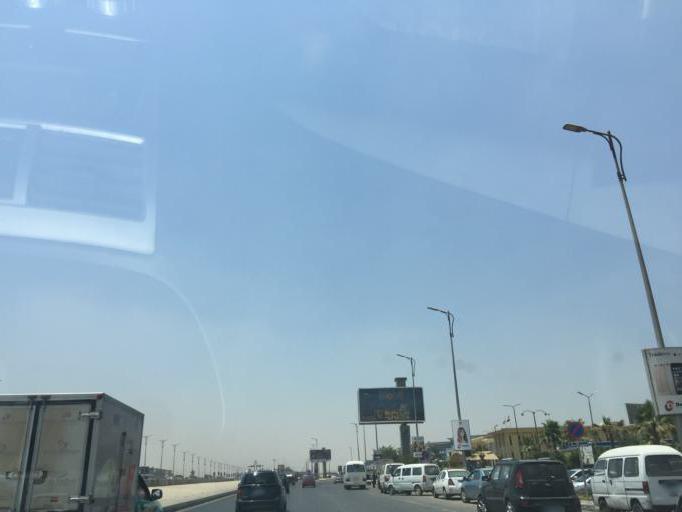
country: EG
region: Al Jizah
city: Awsim
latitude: 30.0627
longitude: 31.0266
